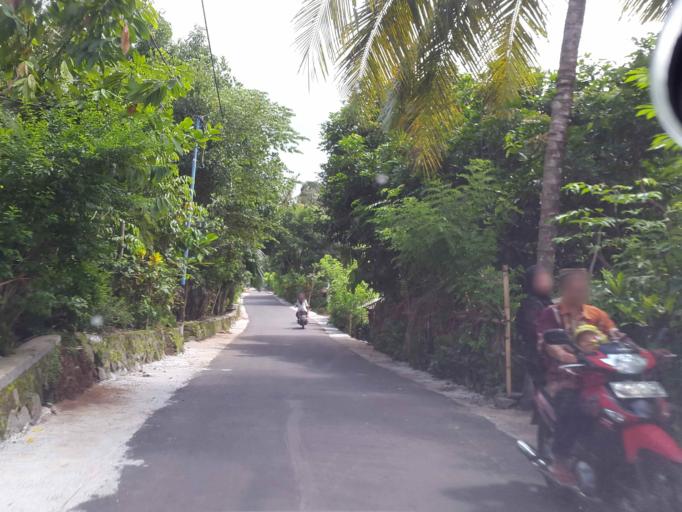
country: ID
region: West Nusa Tenggara
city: Penimbung Barat
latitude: -8.5286
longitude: 116.1555
